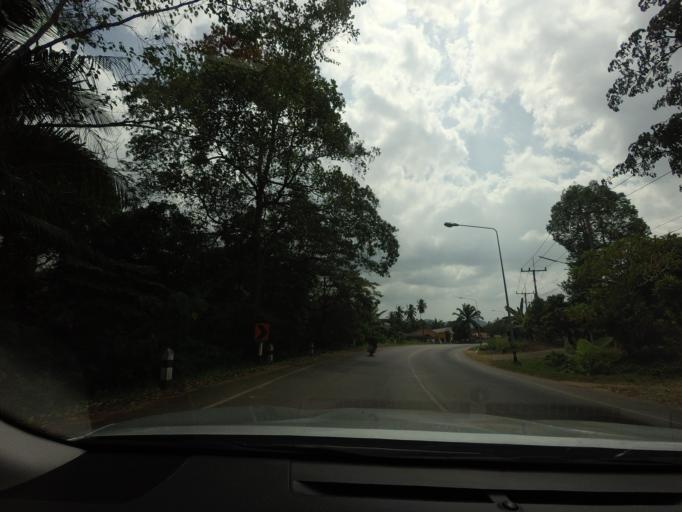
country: TH
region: Phangnga
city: Ban Ao Nang
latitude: 8.1117
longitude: 98.8029
